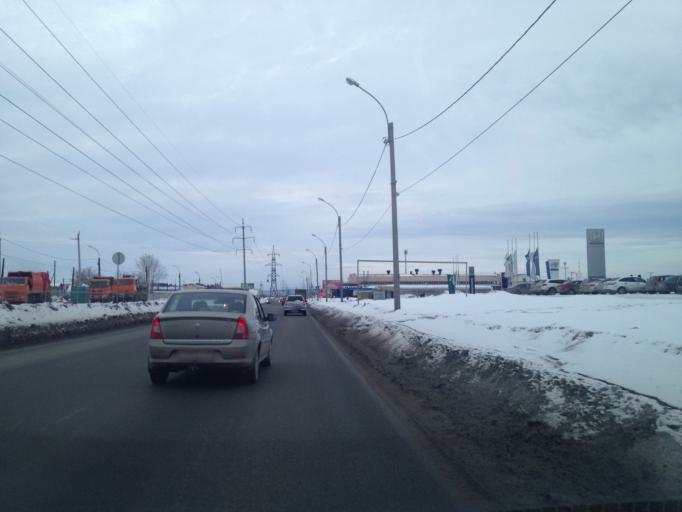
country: RU
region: Sverdlovsk
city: Sovkhoznyy
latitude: 56.7604
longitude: 60.5892
